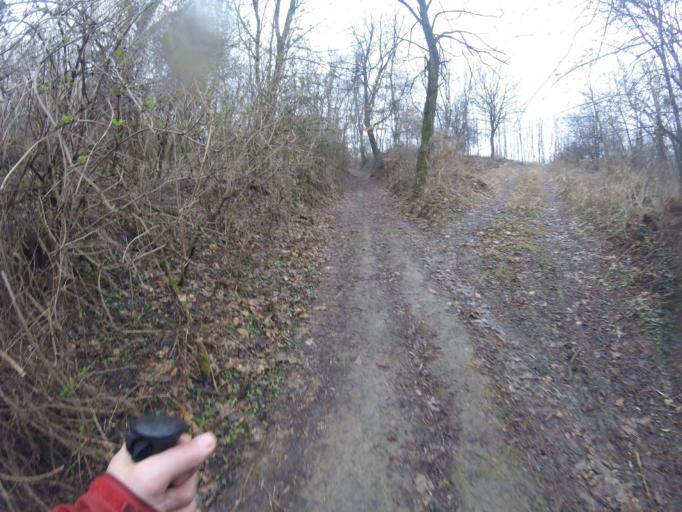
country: HU
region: Gyor-Moson-Sopron
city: Bakonyszentlaszlo
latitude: 47.3610
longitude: 17.8408
